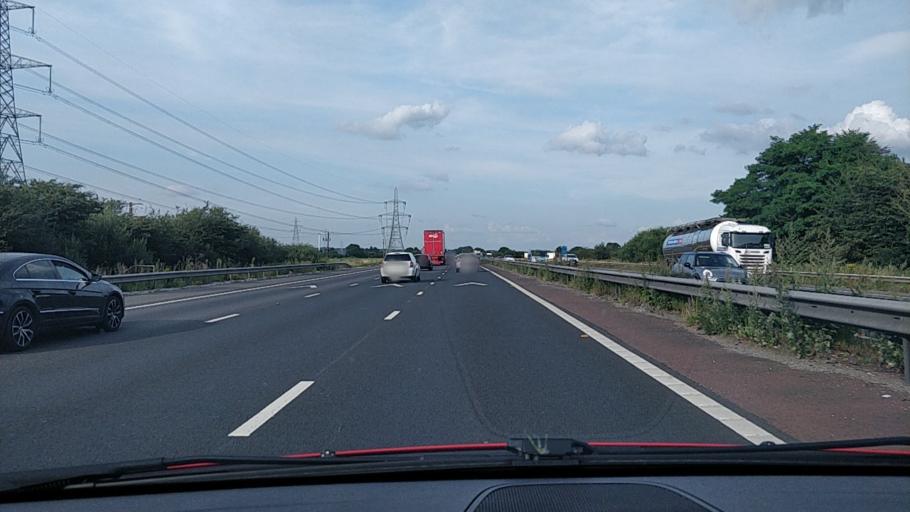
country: GB
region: England
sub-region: Cheshire West and Chester
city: Helsby
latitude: 53.2809
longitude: -2.7661
